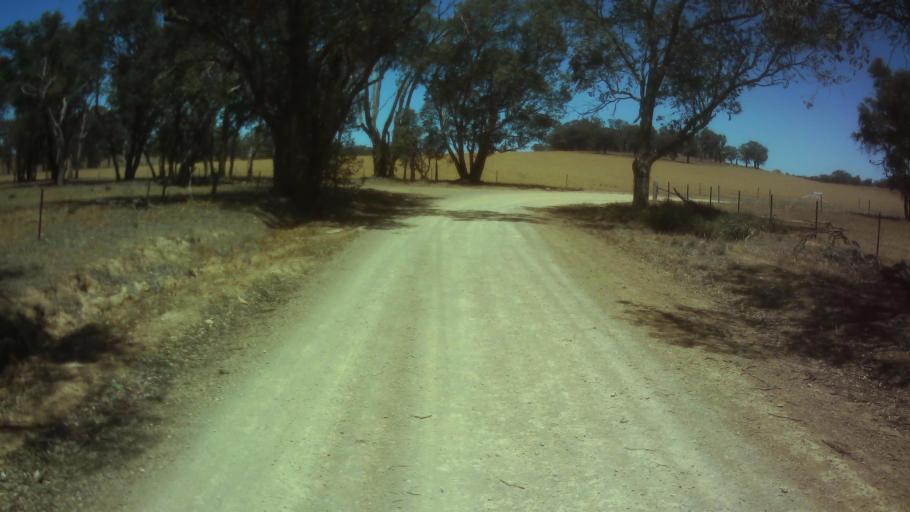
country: AU
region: New South Wales
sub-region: Weddin
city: Grenfell
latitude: -33.9220
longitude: 148.2121
